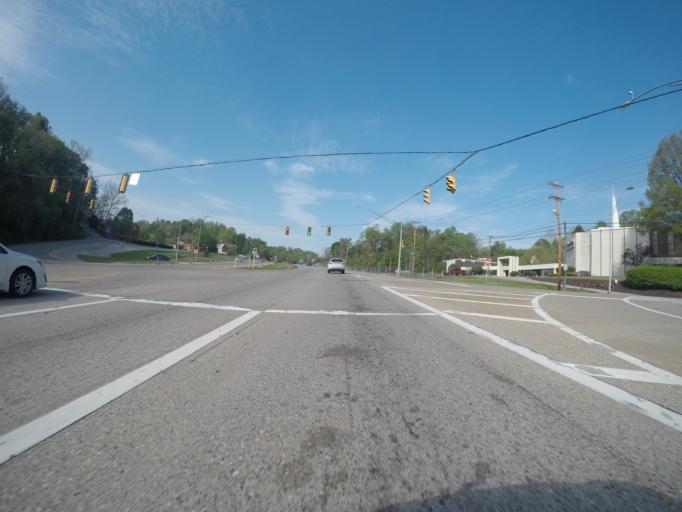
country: US
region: West Virginia
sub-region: Kanawha County
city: South Charleston
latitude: 38.3431
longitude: -81.6761
